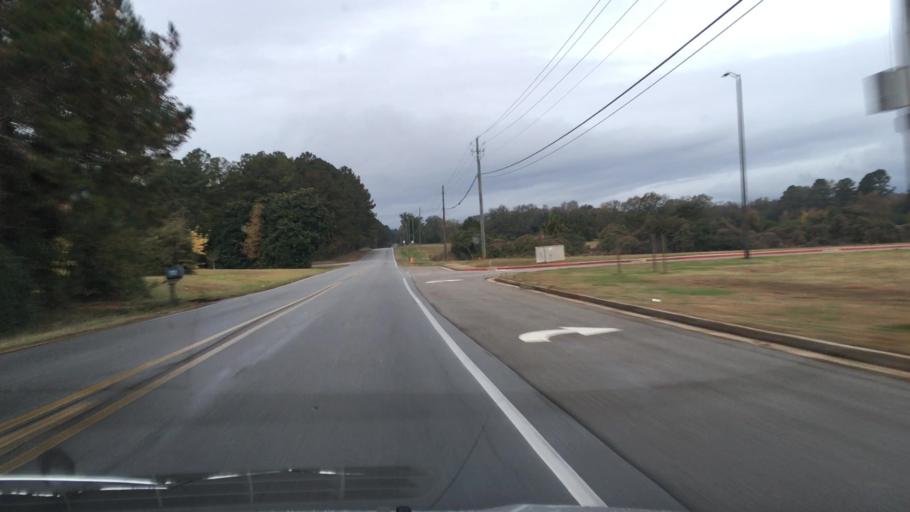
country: US
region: Georgia
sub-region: Henry County
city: Stockbridge
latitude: 33.5320
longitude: -84.1656
